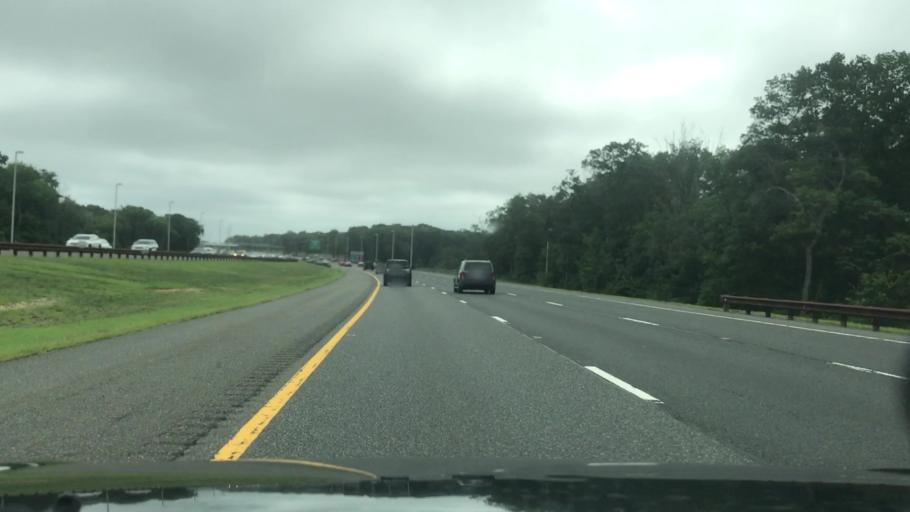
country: US
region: New Jersey
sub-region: Ocean County
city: Leisure Village
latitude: 40.0023
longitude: -74.2026
